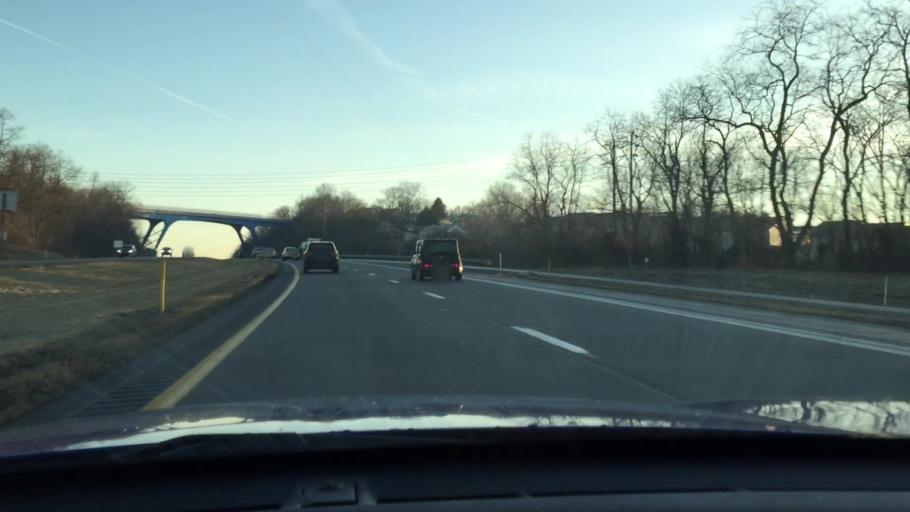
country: US
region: Pennsylvania
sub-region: Washington County
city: Houston
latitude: 40.2482
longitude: -80.1990
